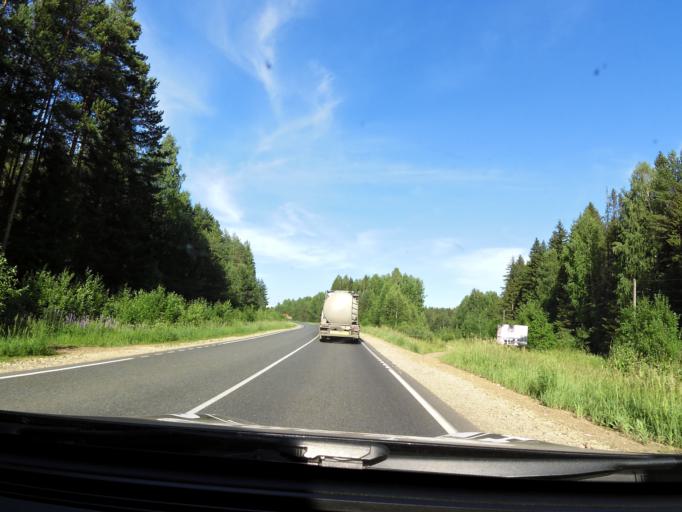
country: RU
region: Kirov
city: Belaya Kholunitsa
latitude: 58.8966
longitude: 50.9183
